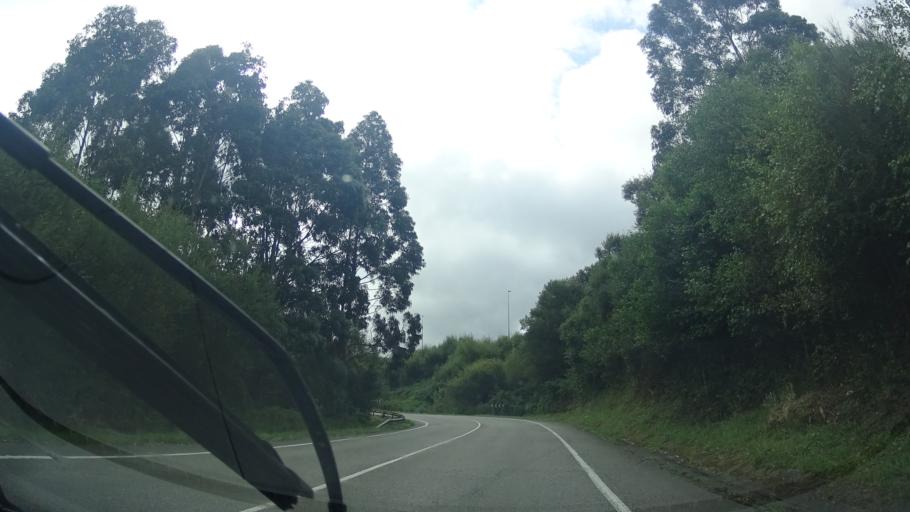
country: ES
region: Asturias
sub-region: Province of Asturias
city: Ribadesella
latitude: 43.4603
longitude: -5.1181
